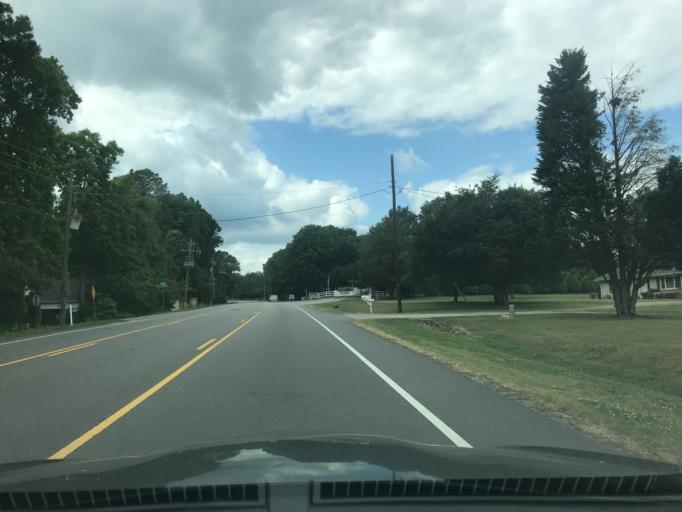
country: US
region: North Carolina
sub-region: Wake County
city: Wake Forest
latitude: 35.8989
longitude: -78.5999
